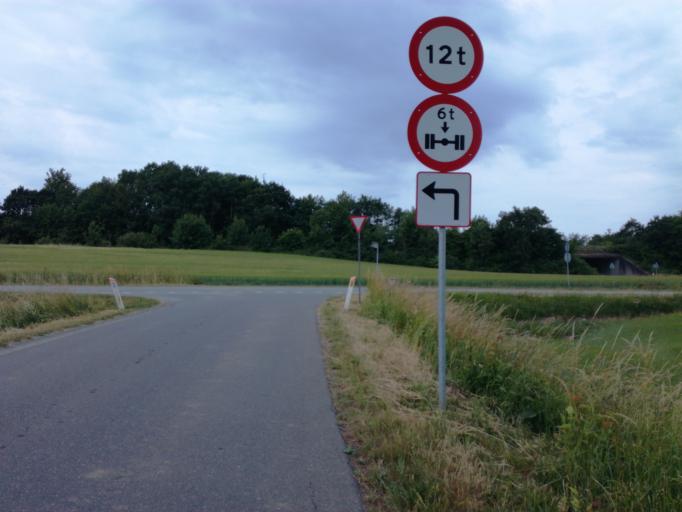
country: DK
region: South Denmark
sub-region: Vejle Kommune
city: Borkop
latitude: 55.6544
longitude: 9.6423
